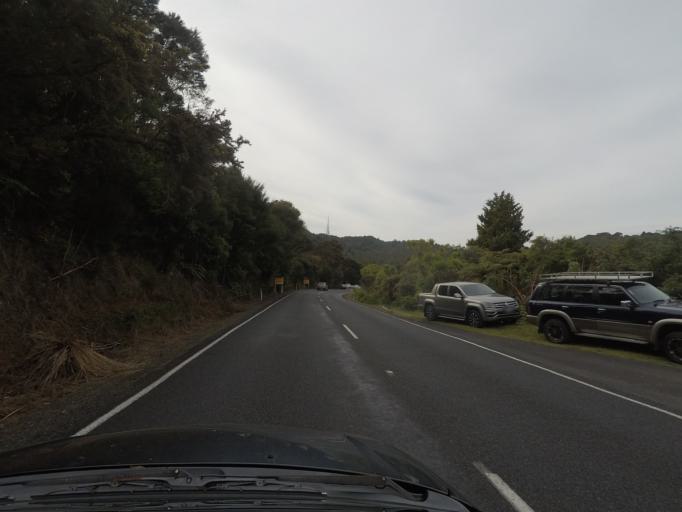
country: NZ
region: Auckland
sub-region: Auckland
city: Titirangi
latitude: -36.9375
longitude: 174.5556
